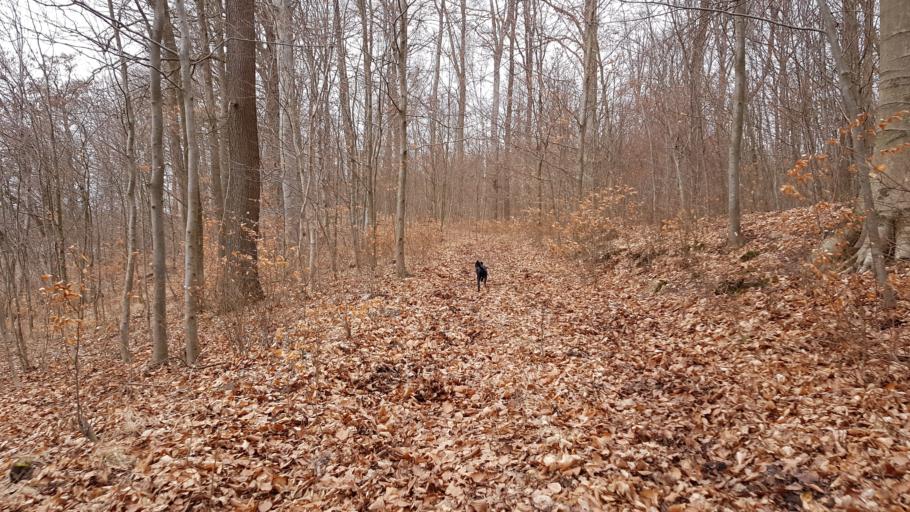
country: PL
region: West Pomeranian Voivodeship
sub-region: Powiat pyrzycki
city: Kozielice
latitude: 53.0786
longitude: 14.7473
